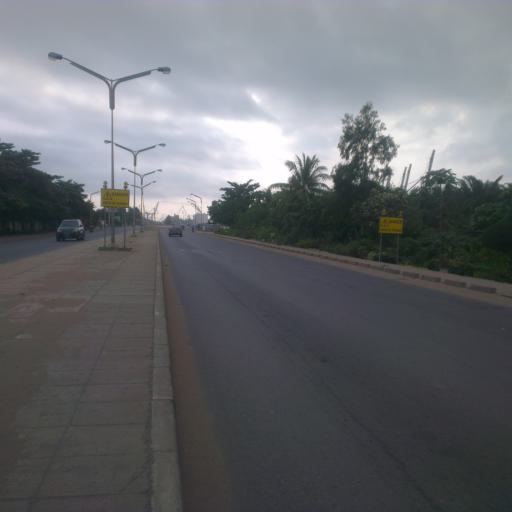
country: TG
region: Maritime
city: Lome
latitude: 6.1383
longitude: 1.2671
